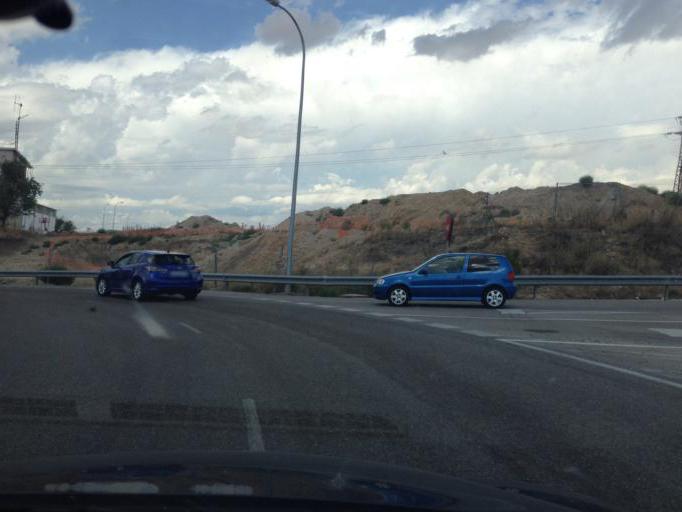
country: ES
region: Madrid
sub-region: Provincia de Madrid
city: San Fernando de Henares
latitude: 40.4558
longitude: -3.5106
